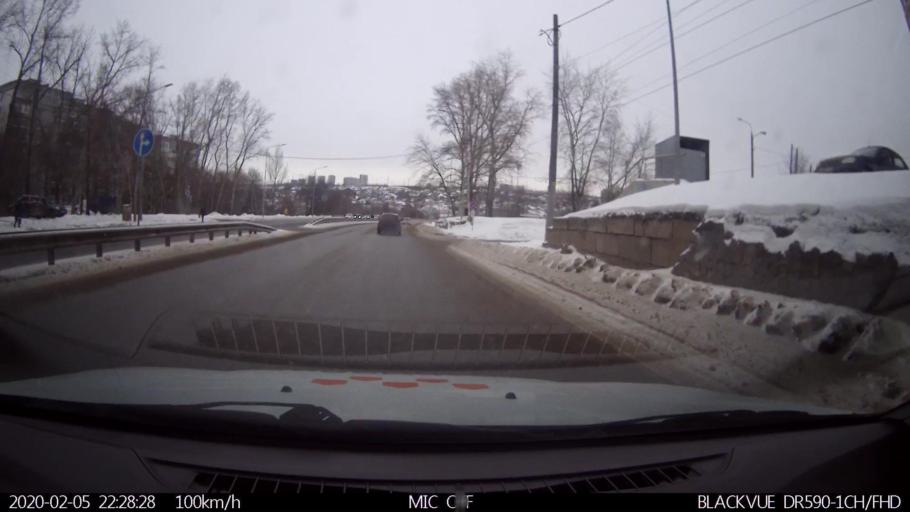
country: RU
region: Nizjnij Novgorod
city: Imeni Stepana Razina
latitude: 54.7573
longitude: 44.1337
